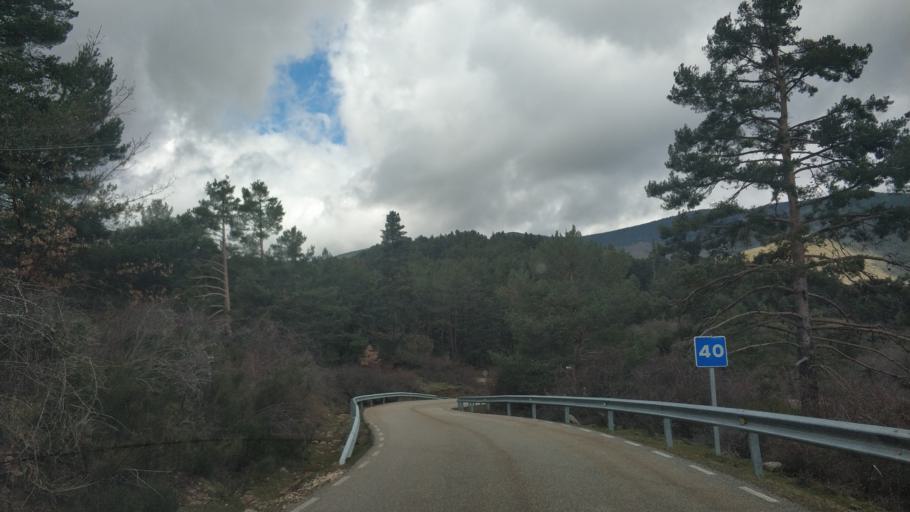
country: ES
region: Castille and Leon
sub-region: Provincia de Burgos
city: Neila
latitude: 42.0560
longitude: -3.0115
